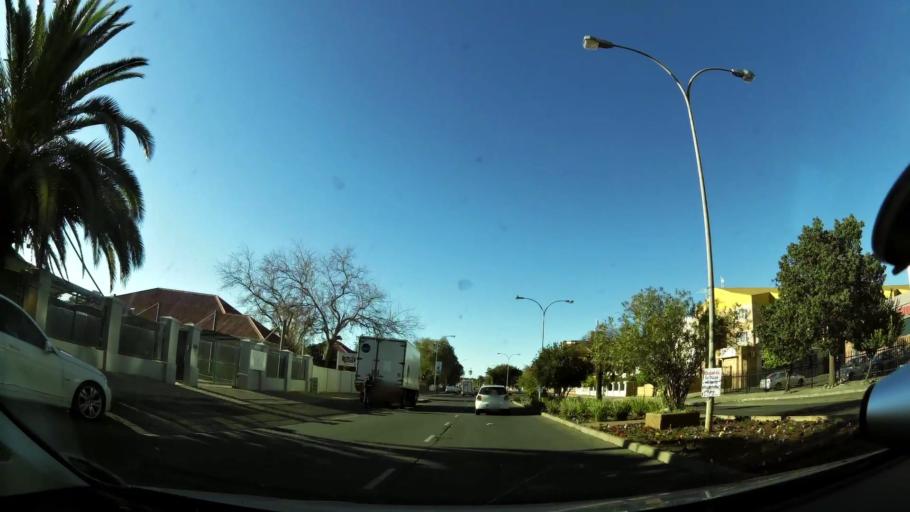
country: ZA
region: Northern Cape
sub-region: Frances Baard District Municipality
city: Kimberley
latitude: -28.7431
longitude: 24.7702
